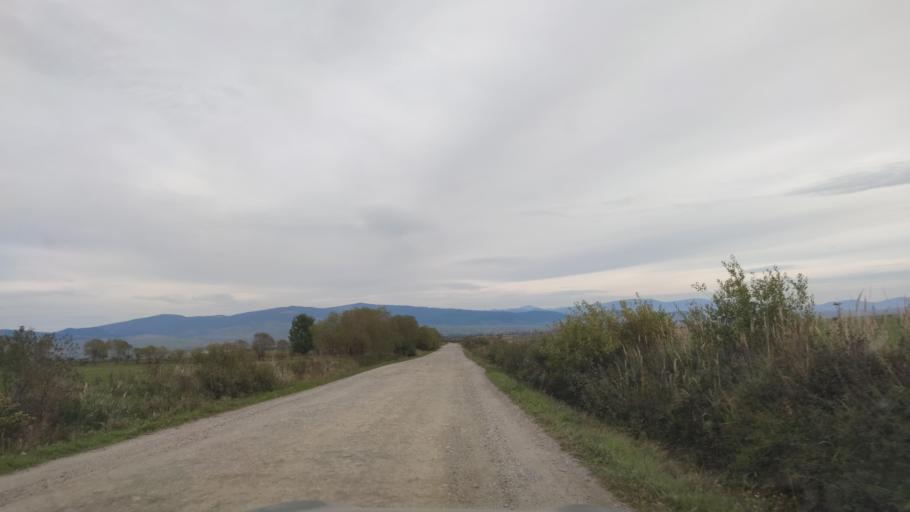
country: RO
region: Harghita
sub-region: Comuna Remetea
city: Remetea
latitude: 46.8093
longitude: 25.4000
